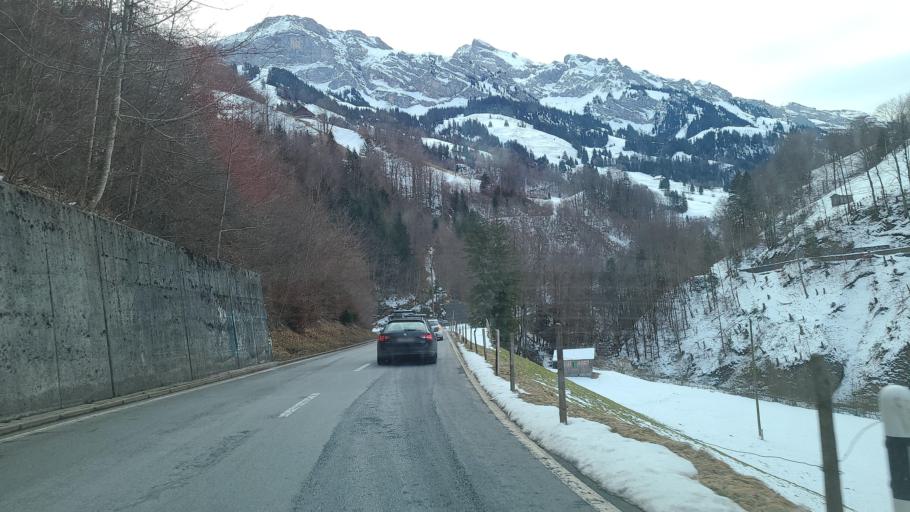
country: CH
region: Obwalden
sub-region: Obwalden
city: Kerns
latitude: 46.8531
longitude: 8.2953
